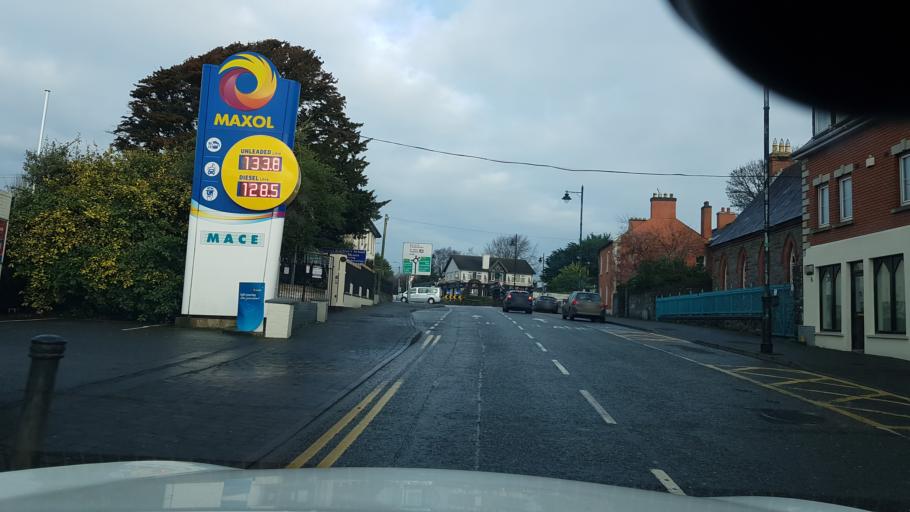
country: IE
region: Leinster
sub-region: An Mhi
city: Navan
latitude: 53.6578
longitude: -6.6798
